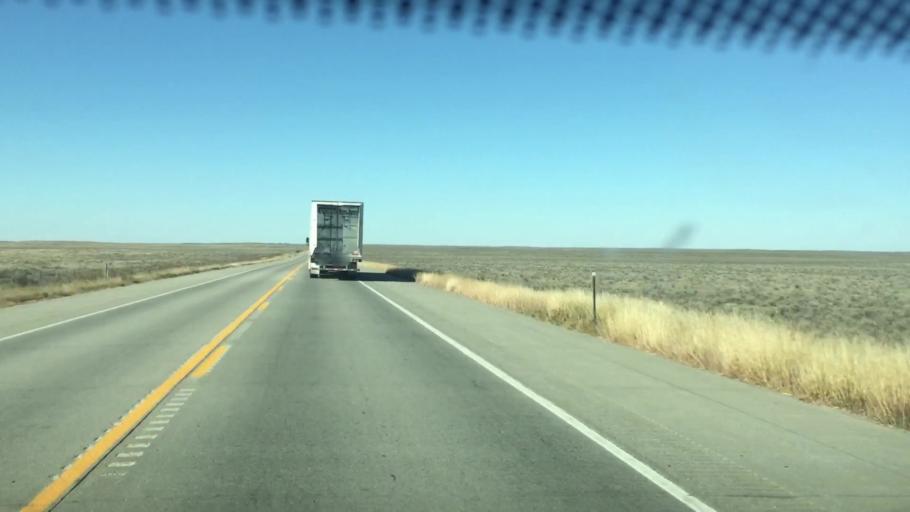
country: US
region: Colorado
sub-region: Kiowa County
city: Eads
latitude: 38.5489
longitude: -102.7859
